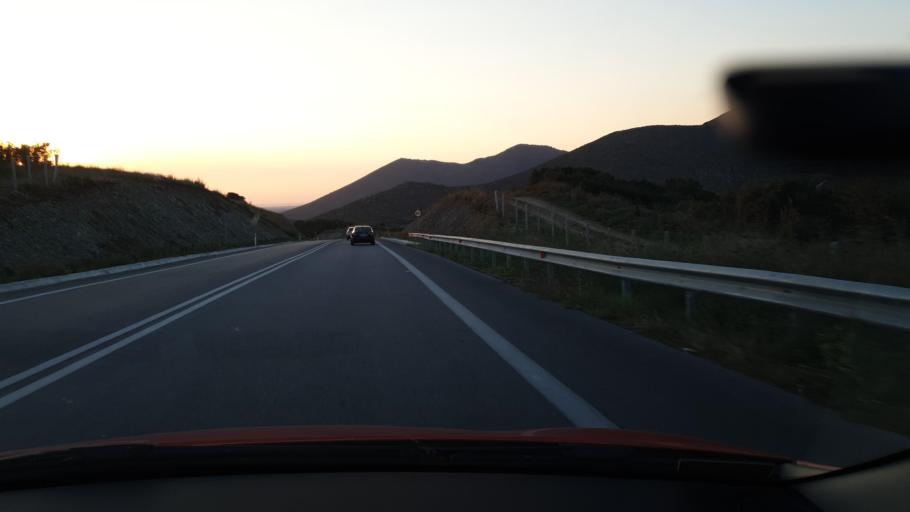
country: GR
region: Central Macedonia
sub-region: Nomos Chalkidikis
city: Galatista
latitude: 40.4628
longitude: 23.2218
